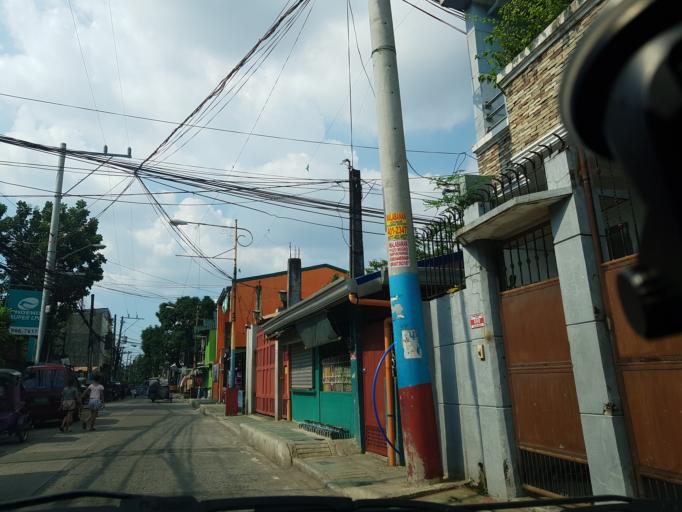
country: PH
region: Calabarzon
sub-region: Province of Rizal
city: Pateros
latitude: 14.5590
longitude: 121.0899
